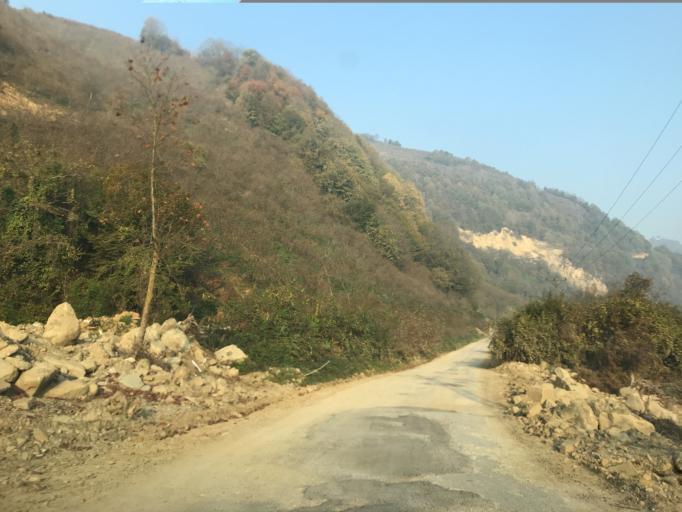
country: TR
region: Duzce
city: Cumayeri
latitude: 40.9183
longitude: 30.9304
